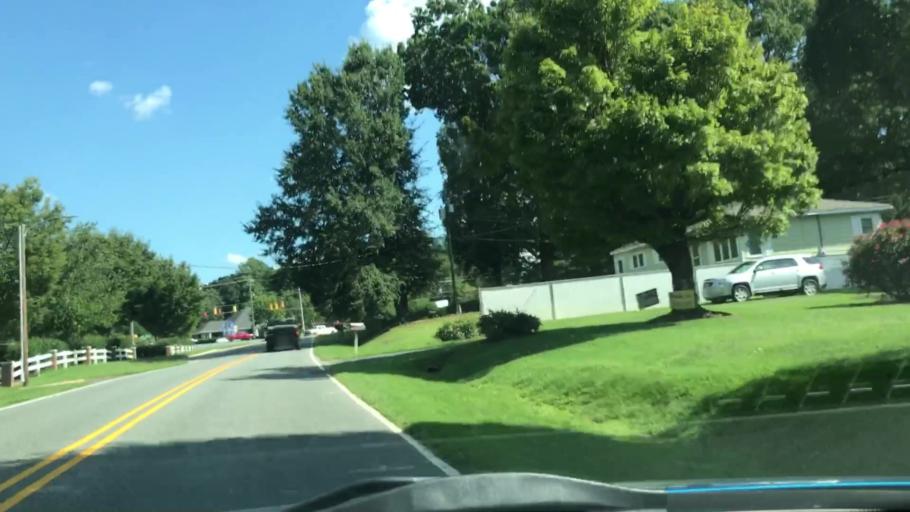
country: US
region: North Carolina
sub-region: Randolph County
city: Asheboro
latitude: 35.7462
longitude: -79.8088
